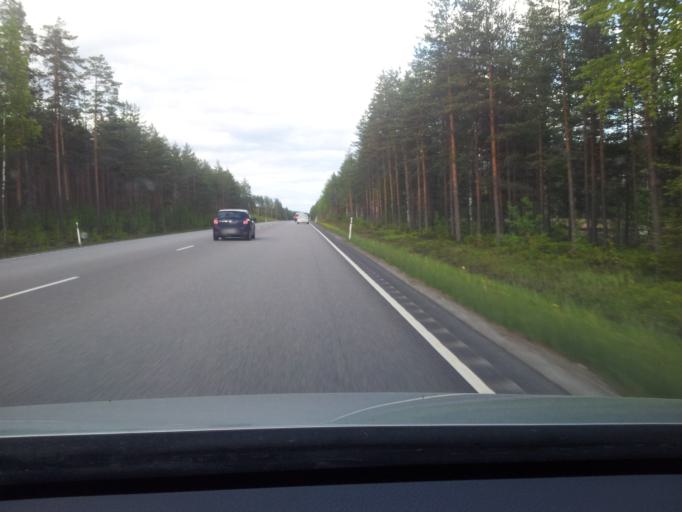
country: FI
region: South Karelia
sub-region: Lappeenranta
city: Taavetti
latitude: 60.9179
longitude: 27.4815
